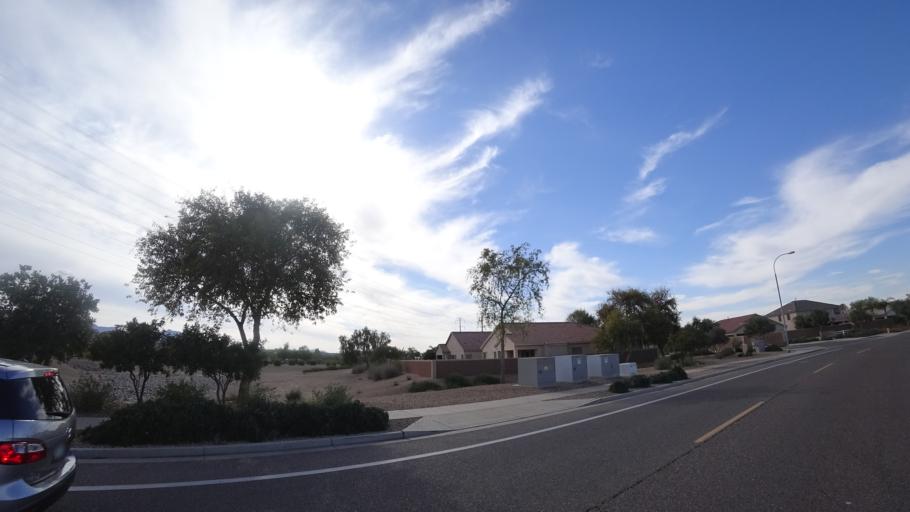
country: US
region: Arizona
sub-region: Maricopa County
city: Tolleson
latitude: 33.4144
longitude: -112.2810
